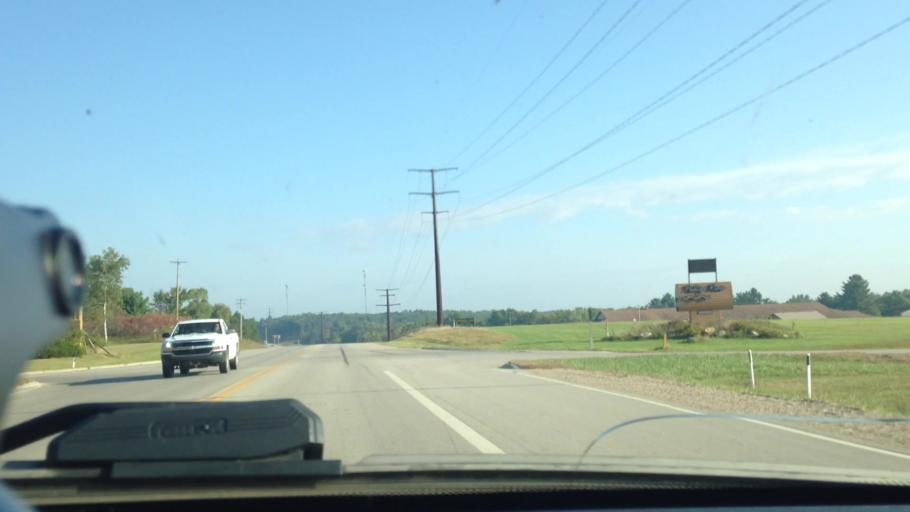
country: US
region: Wisconsin
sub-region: Marinette County
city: Peshtigo
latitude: 45.2026
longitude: -87.9943
